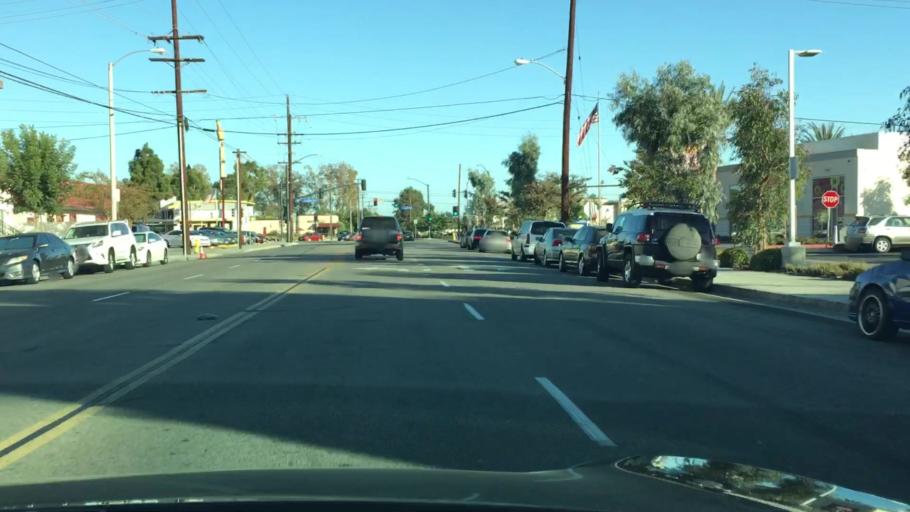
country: US
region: California
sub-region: Los Angeles County
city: Downey
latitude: 33.9550
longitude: -118.1148
